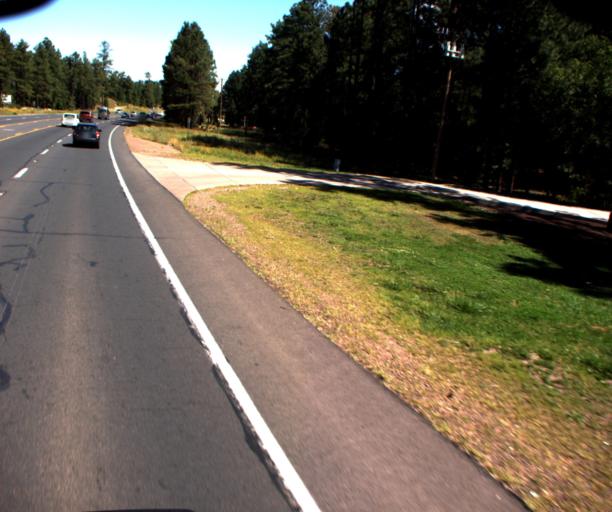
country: US
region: Arizona
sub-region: Navajo County
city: Show Low
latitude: 34.2219
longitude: -110.0293
